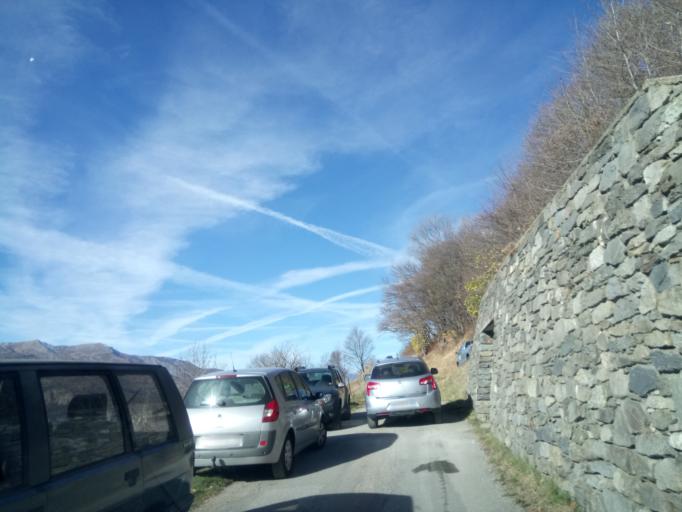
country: FR
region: Rhone-Alpes
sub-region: Departement de la Savoie
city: Saint-Michel-de-Maurienne
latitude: 45.2249
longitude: 6.4894
